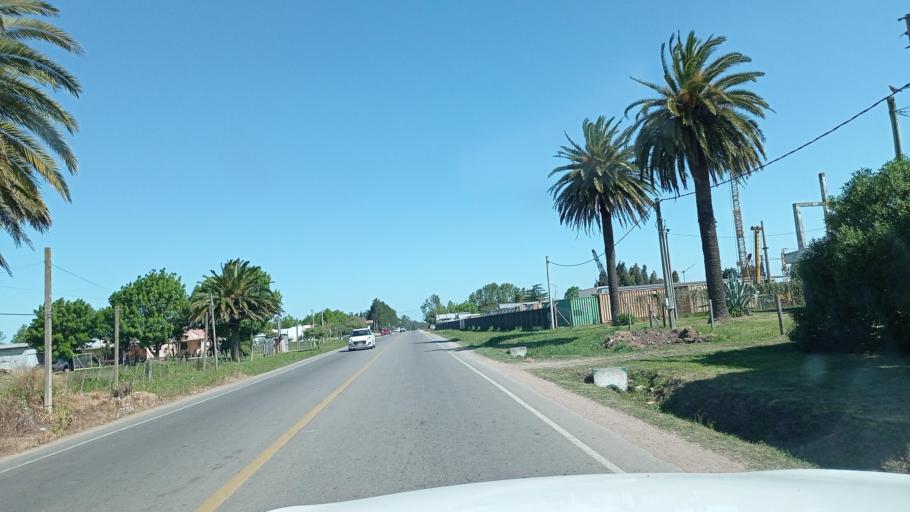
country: UY
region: Canelones
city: La Paz
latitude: -34.7878
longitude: -56.1662
